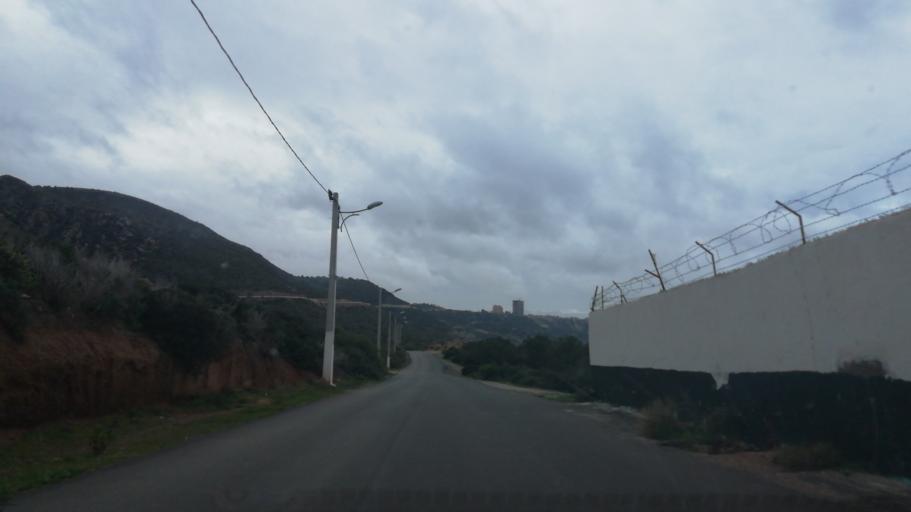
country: DZ
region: Oran
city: Bir el Djir
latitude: 35.7749
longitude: -0.5154
